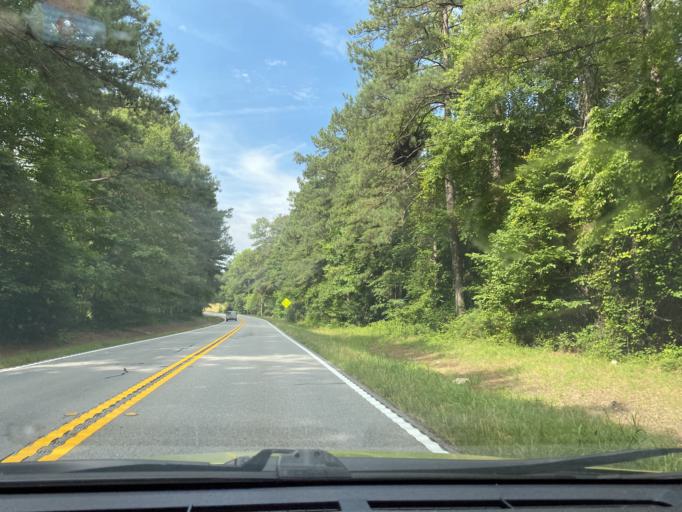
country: US
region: Georgia
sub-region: Fayette County
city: Peachtree City
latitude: 33.3173
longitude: -84.6519
